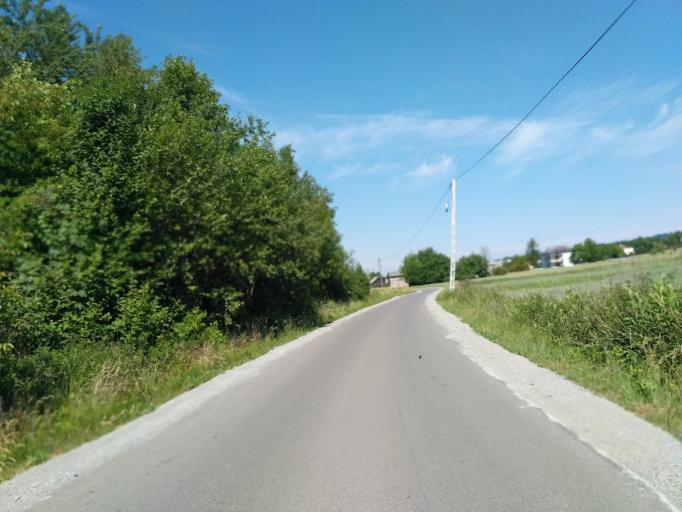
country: PL
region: Subcarpathian Voivodeship
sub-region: Powiat krosnienski
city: Korczyna
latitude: 49.7182
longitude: 21.7804
